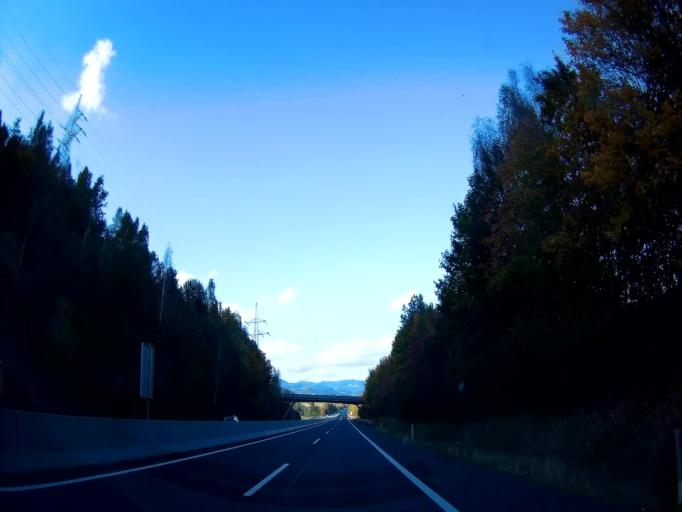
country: AT
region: Carinthia
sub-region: Politischer Bezirk Wolfsberg
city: Sankt Andrae
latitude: 46.7630
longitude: 14.8143
